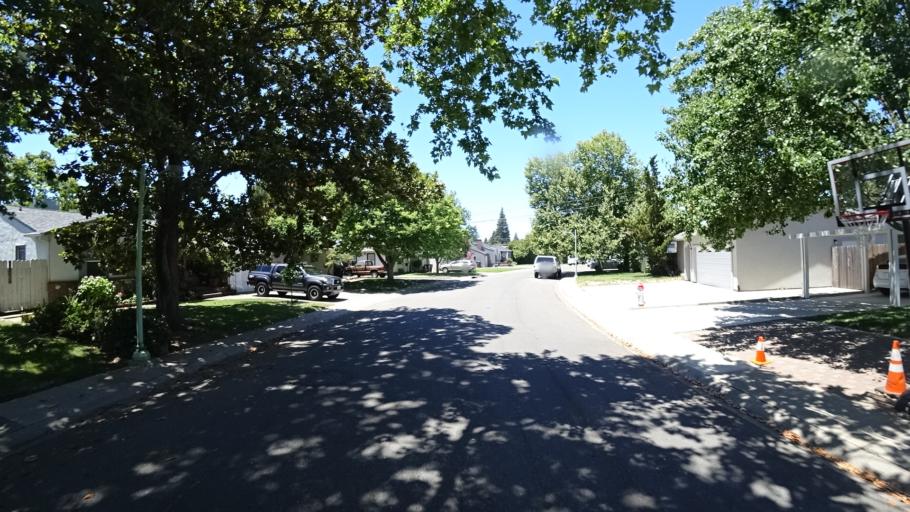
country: US
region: California
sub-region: Sacramento County
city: Parkway
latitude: 38.5306
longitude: -121.4939
